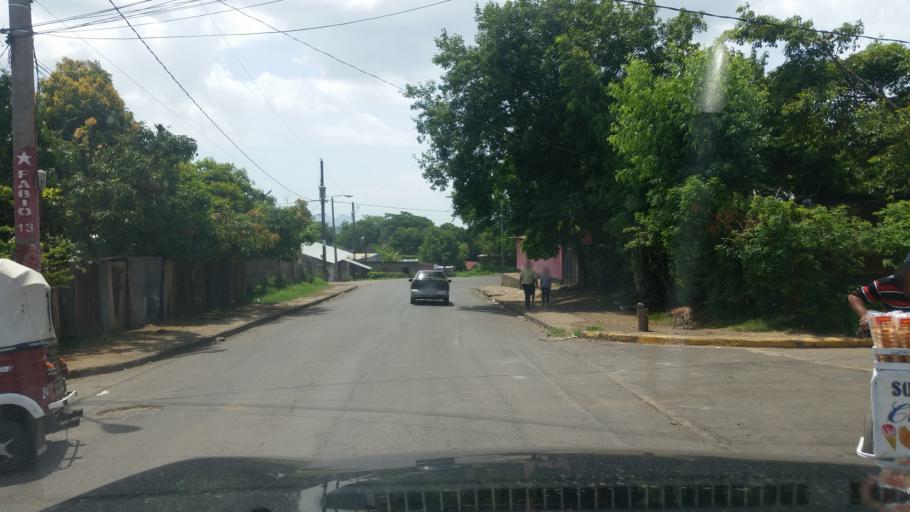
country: NI
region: Managua
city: Managua
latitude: 12.1089
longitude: -86.2380
